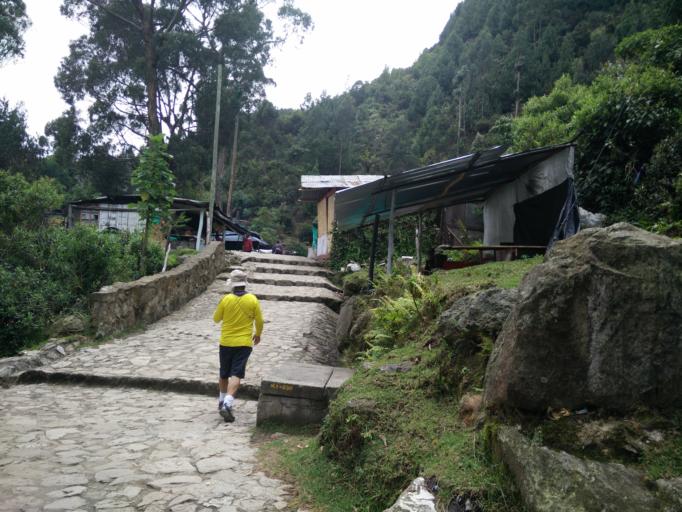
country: CO
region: Bogota D.C.
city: Bogota
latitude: 4.6089
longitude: -74.0580
